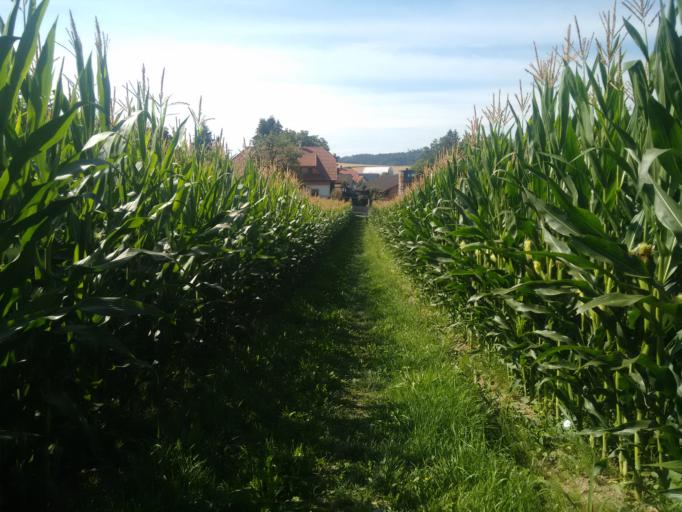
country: AT
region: Upper Austria
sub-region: Politischer Bezirk Grieskirchen
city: Bad Schallerbach
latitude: 48.1951
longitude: 13.9432
